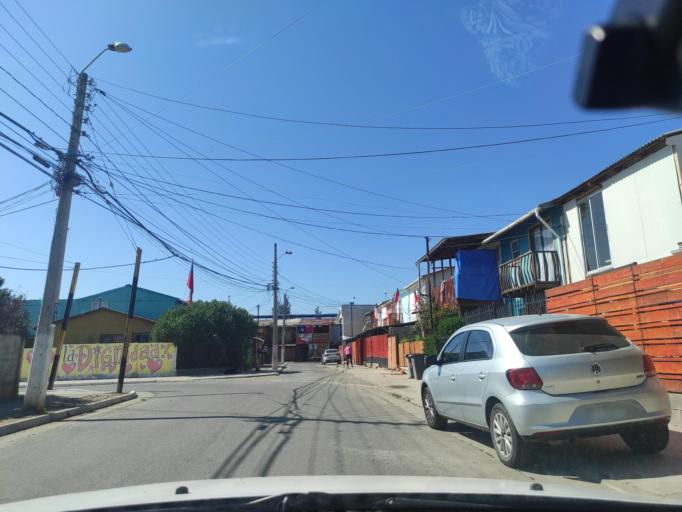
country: CL
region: Valparaiso
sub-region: Provincia de Marga Marga
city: Limache
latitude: -33.0199
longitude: -71.2640
